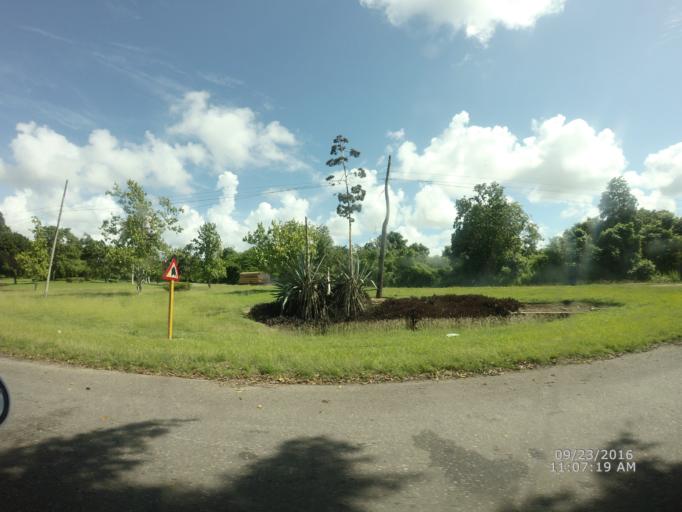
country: CU
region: Mayabeque
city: Jamaica
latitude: 23.0148
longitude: -82.2276
